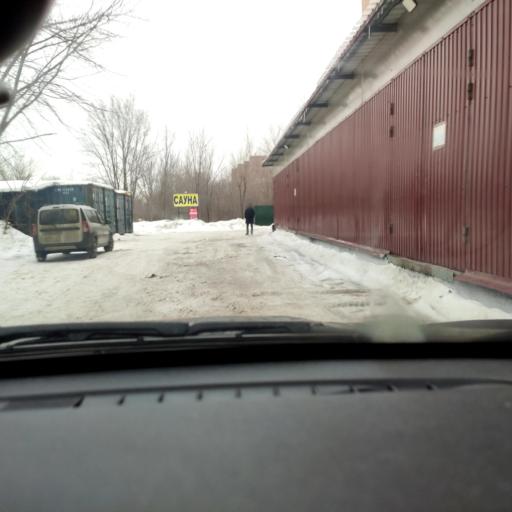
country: RU
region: Samara
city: Tol'yatti
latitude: 53.5460
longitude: 49.2911
